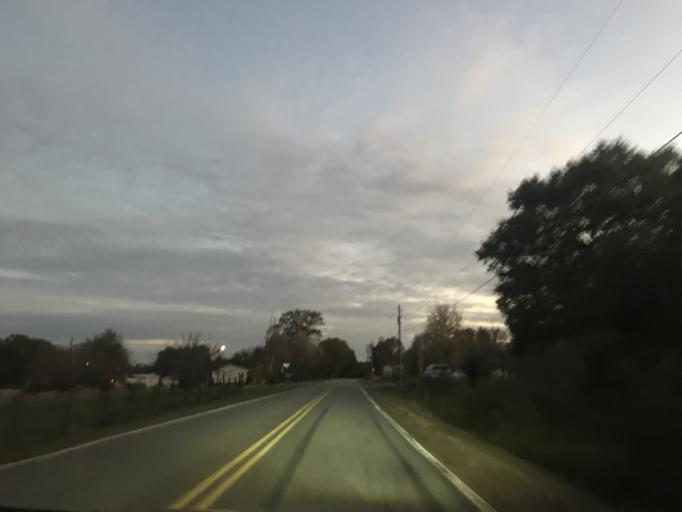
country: US
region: South Carolina
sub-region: Spartanburg County
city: Mayo
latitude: 35.0592
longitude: -81.8927
